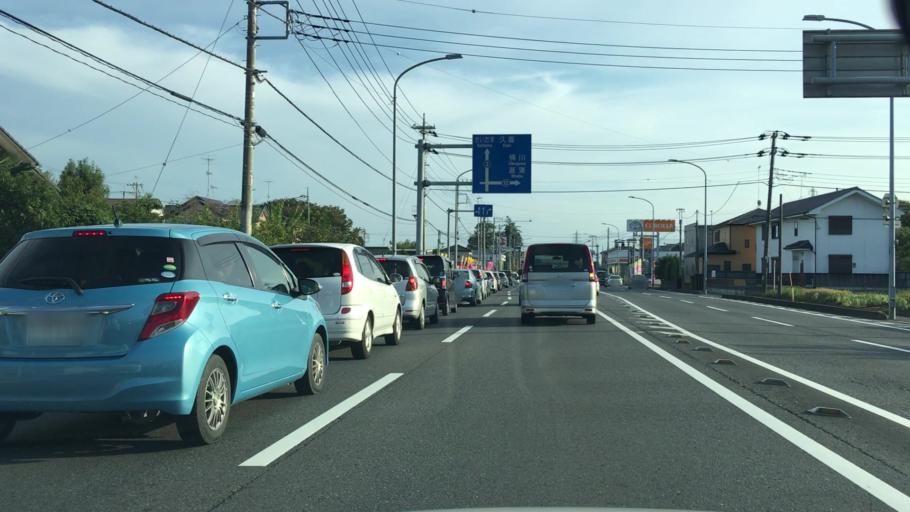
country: JP
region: Saitama
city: Kukichuo
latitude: 36.0951
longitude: 139.6753
